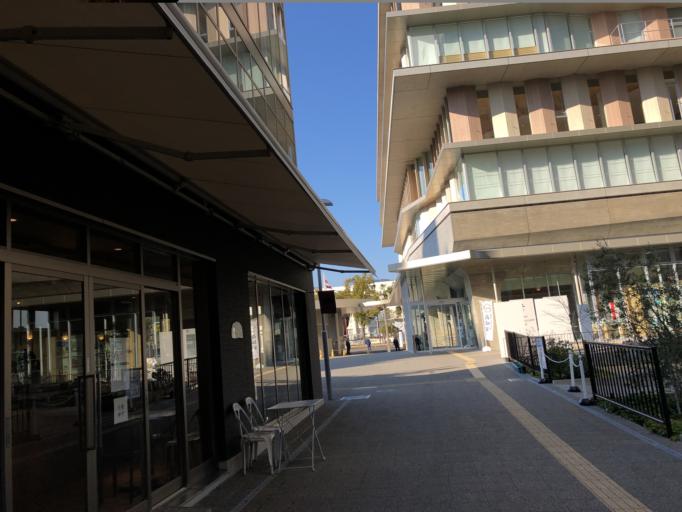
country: JP
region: Kochi
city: Kochi-shi
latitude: 33.5604
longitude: 133.5369
